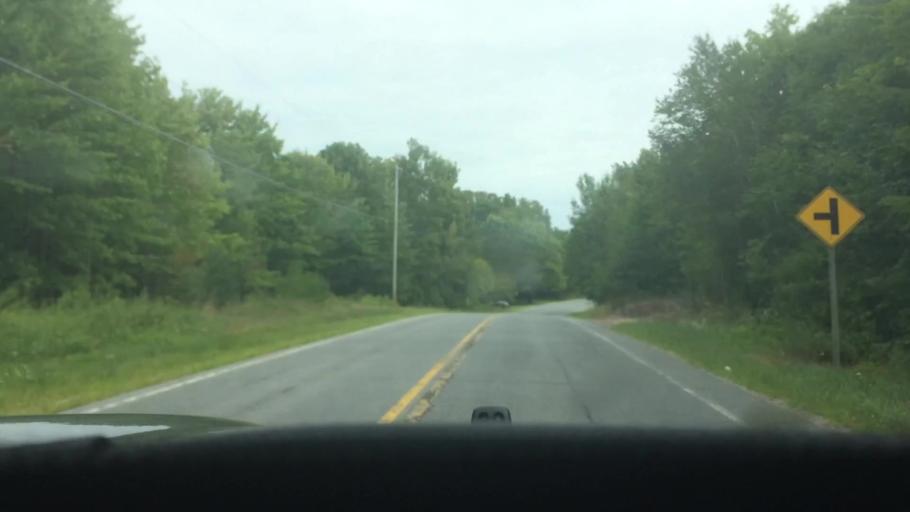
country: US
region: New York
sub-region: St. Lawrence County
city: Canton
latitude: 44.5065
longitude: -75.2123
